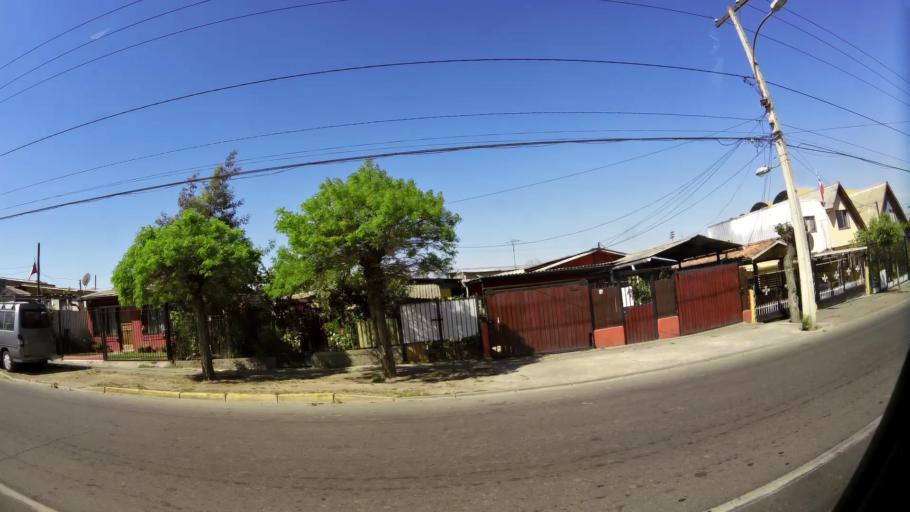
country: CL
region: Santiago Metropolitan
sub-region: Provincia de Santiago
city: Lo Prado
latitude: -33.5041
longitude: -70.7293
